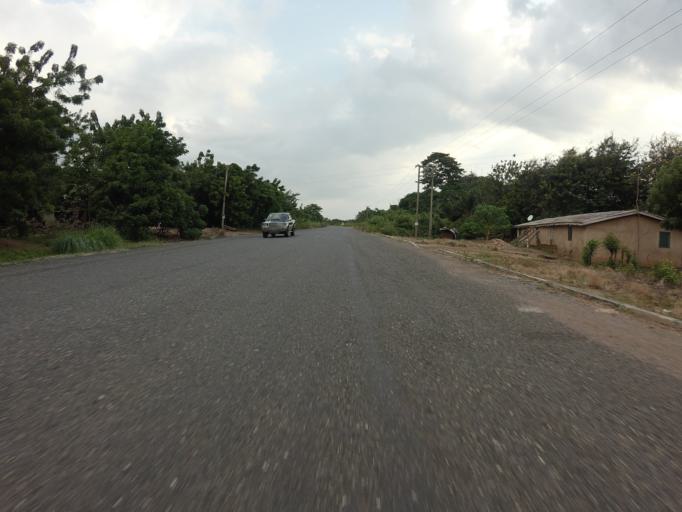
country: GH
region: Volta
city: Ho
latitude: 6.5038
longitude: 0.4887
